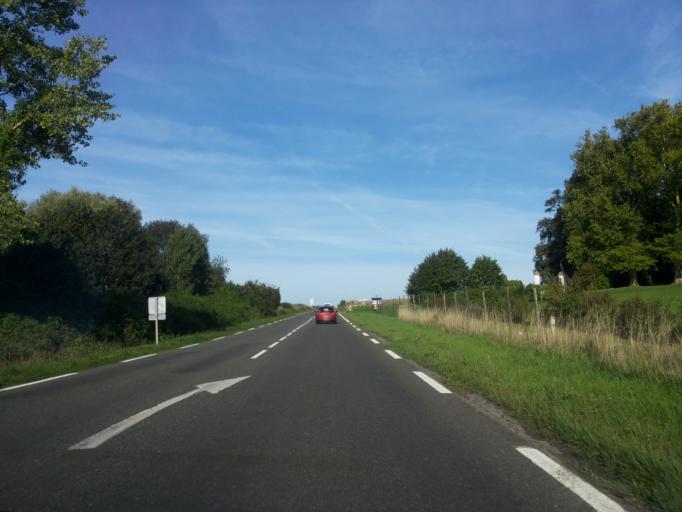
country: FR
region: Picardie
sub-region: Departement de l'Aisne
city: Charmes
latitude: 49.6356
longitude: 3.4101
